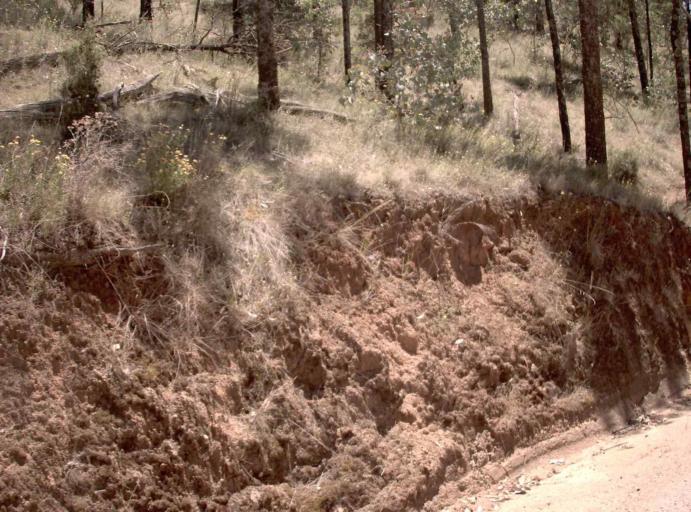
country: AU
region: New South Wales
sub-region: Snowy River
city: Jindabyne
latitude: -36.9272
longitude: 148.3858
